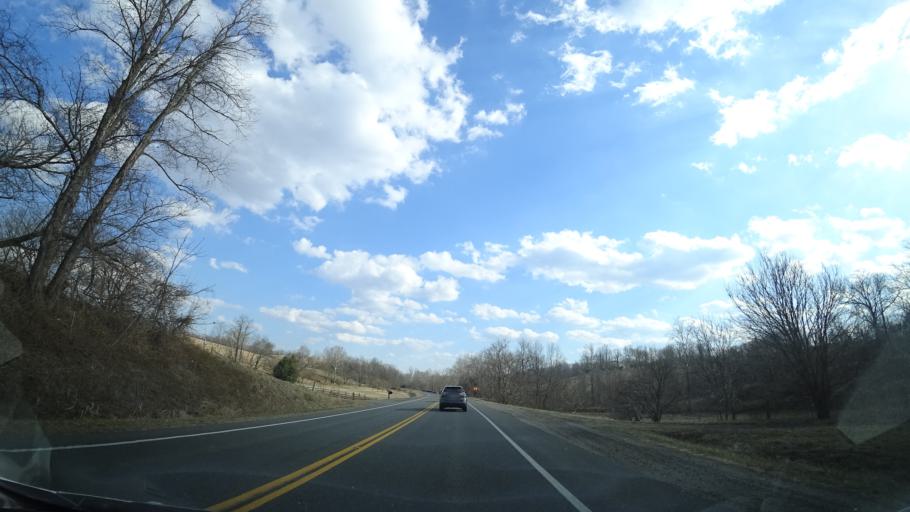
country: US
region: Virginia
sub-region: Fauquier County
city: Marshall
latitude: 38.9284
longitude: -77.9315
